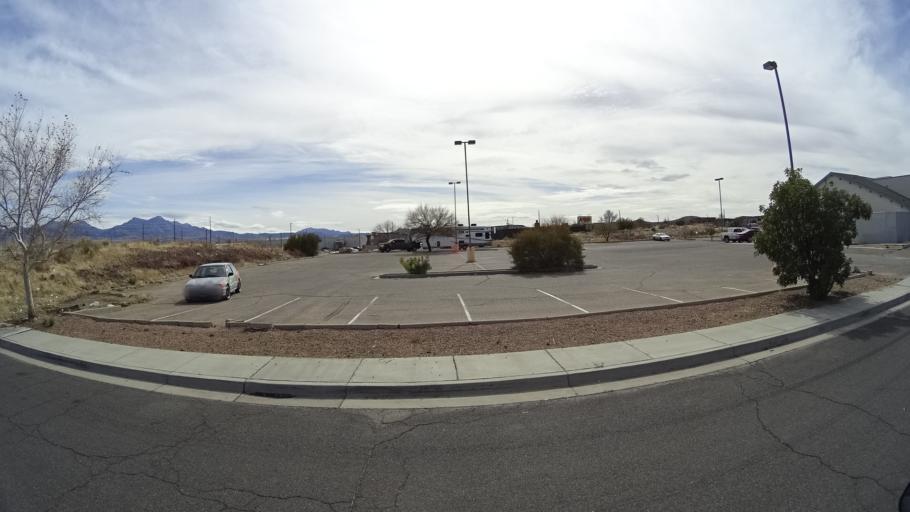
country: US
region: Arizona
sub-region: Mohave County
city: New Kingman-Butler
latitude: 35.2269
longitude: -114.0350
